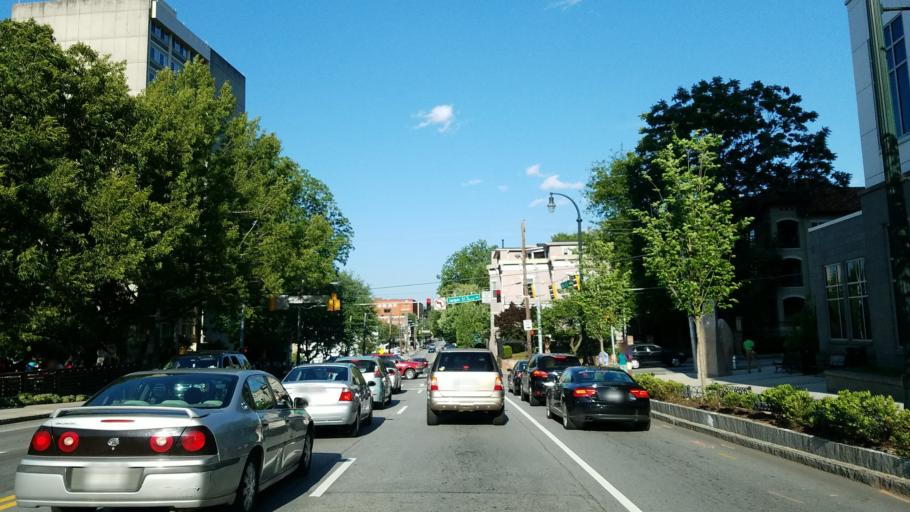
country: US
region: Georgia
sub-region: Fulton County
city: Atlanta
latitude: 33.7816
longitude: -84.3831
